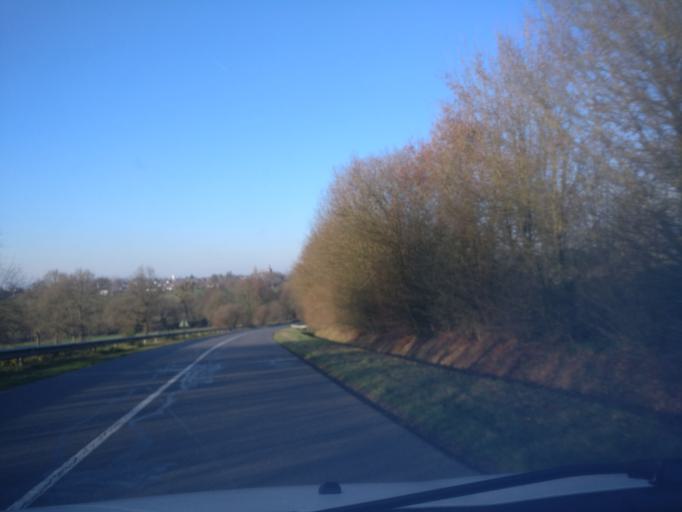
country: FR
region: Brittany
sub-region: Departement d'Ille-et-Vilaine
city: Livre-sur-Changeon
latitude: 48.2088
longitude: -1.3368
